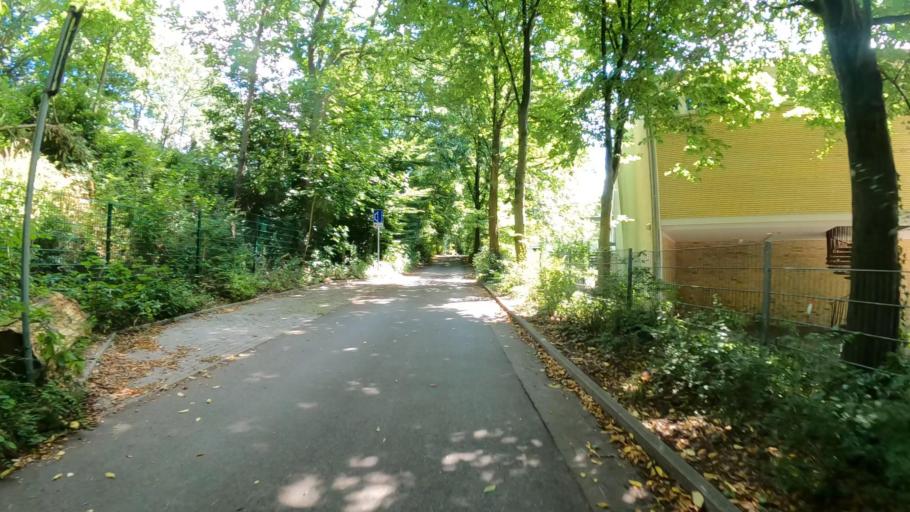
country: DE
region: Hamburg
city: Ohlsdorf
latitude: 53.6290
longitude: 10.0316
